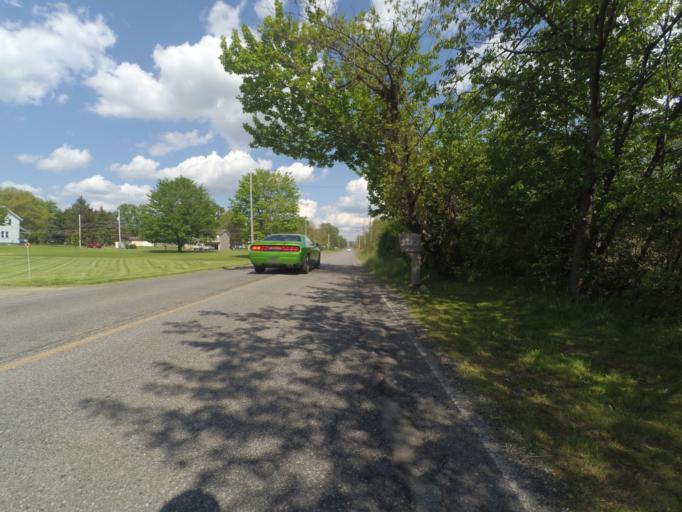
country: US
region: Ohio
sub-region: Trumbull County
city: Mineral Ridge
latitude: 41.1340
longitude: -80.7545
